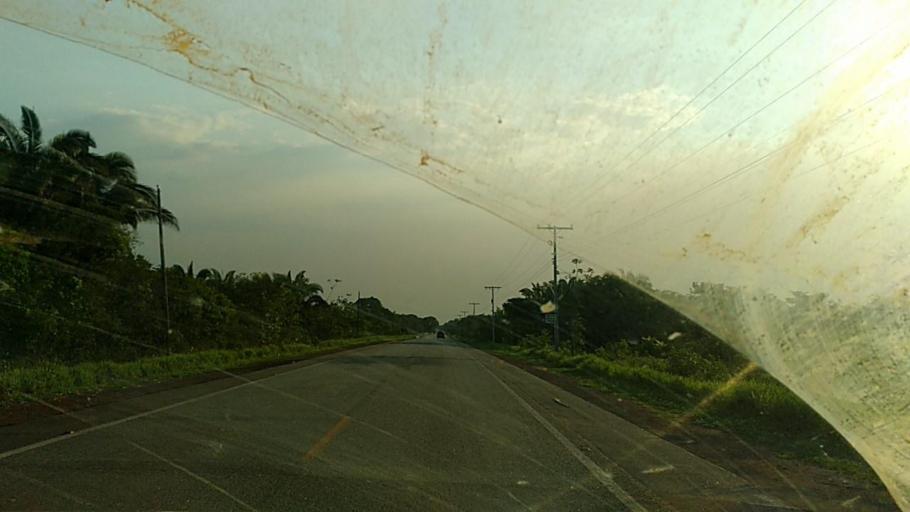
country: BR
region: Amazonas
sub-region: Humaita
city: Humaita
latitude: -7.8067
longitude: -63.1789
